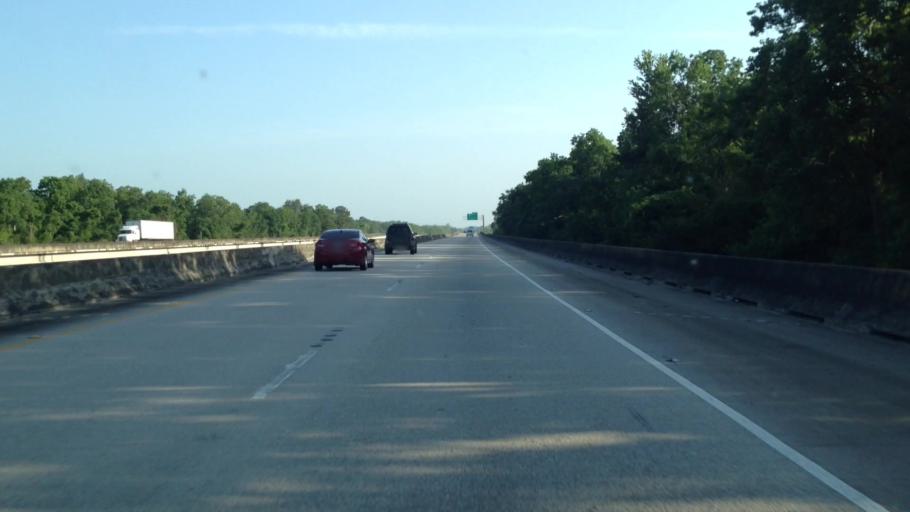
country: US
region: Louisiana
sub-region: Tangipahoa Parish
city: Ponchatoula
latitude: 30.3929
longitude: -90.4287
